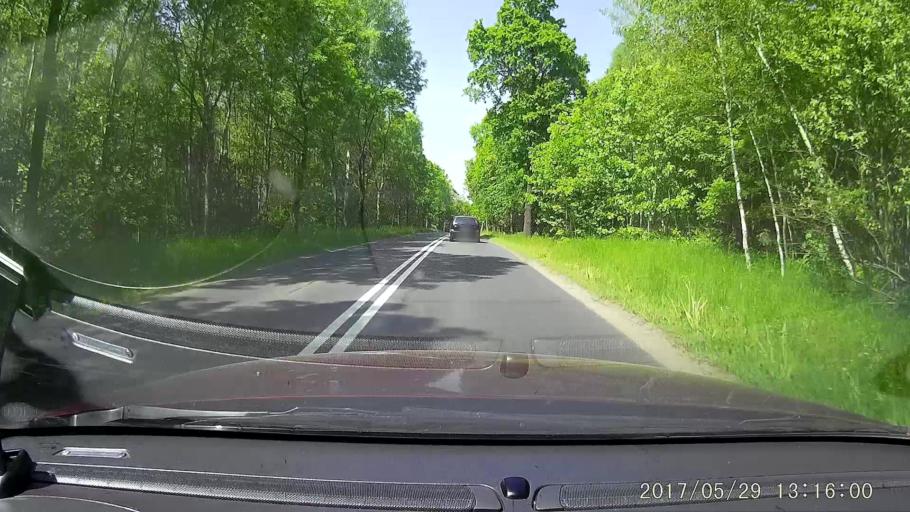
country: PL
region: Lower Silesian Voivodeship
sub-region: Powiat lwowecki
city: Lubomierz
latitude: 50.9920
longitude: 15.4786
